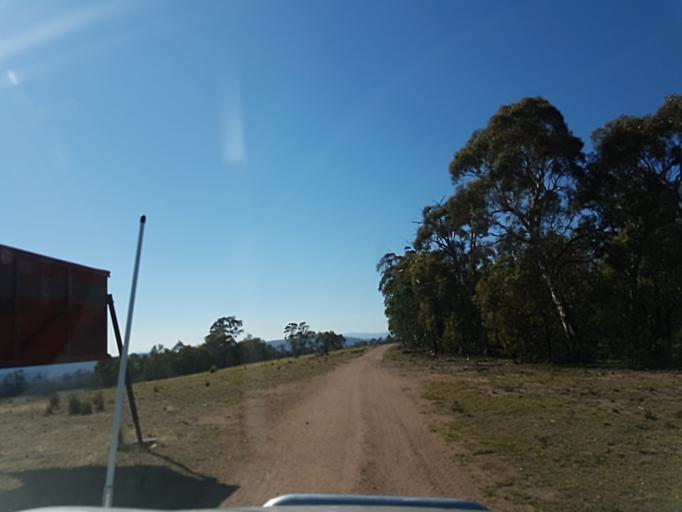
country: AU
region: New South Wales
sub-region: Snowy River
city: Jindabyne
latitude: -37.0386
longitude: 148.2810
